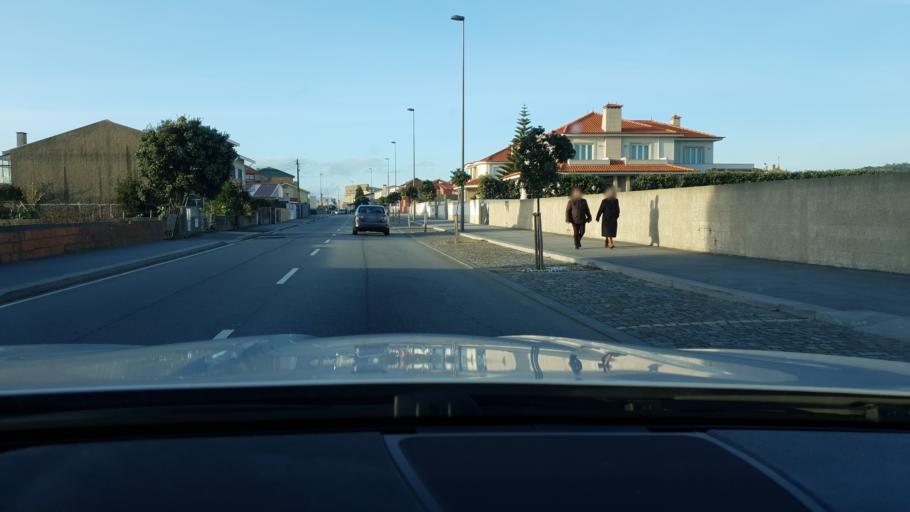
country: PT
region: Porto
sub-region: Matosinhos
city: Lavra
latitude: 41.2354
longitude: -8.7213
